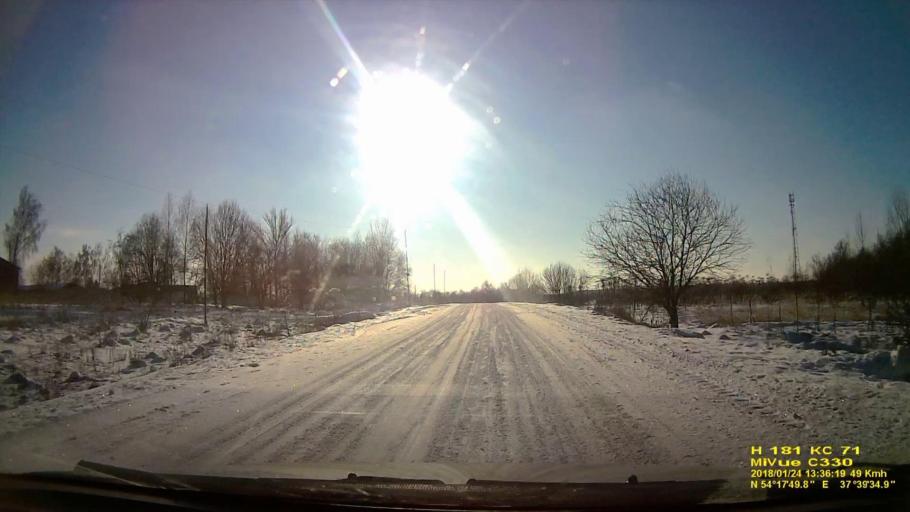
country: RU
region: Tula
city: Gorelki
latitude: 54.2970
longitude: 37.6596
